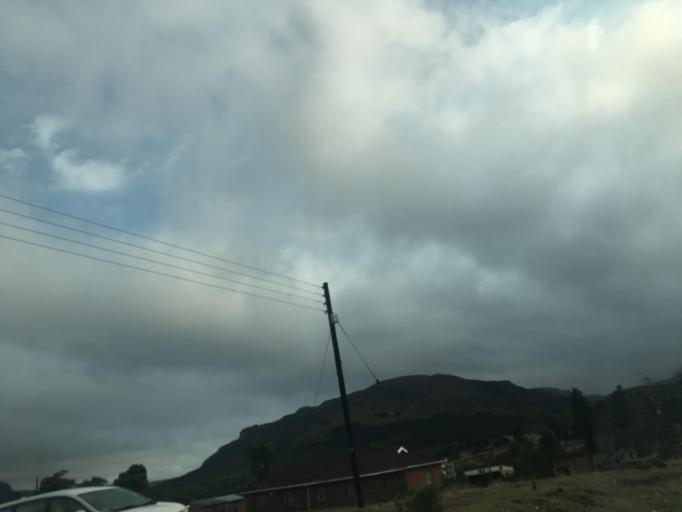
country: ZA
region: Eastern Cape
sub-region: Chris Hani District Municipality
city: Cala
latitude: -31.5198
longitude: 27.7018
